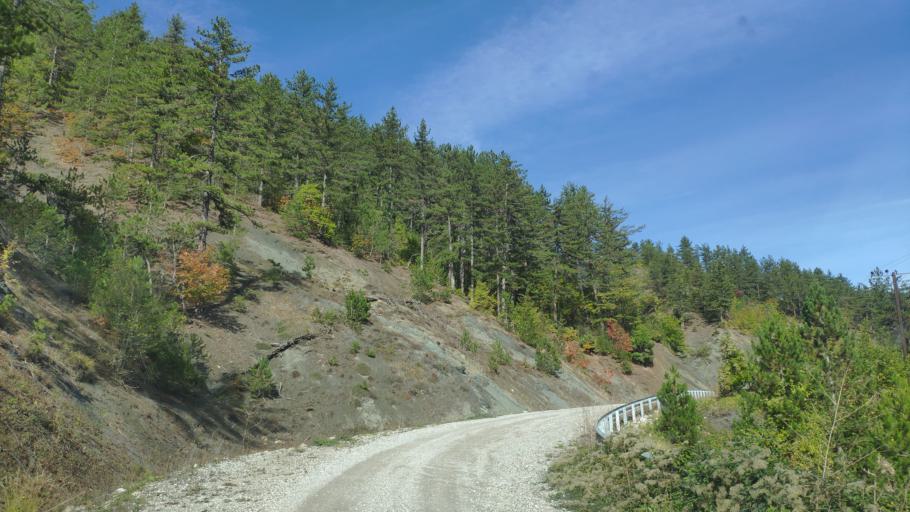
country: AL
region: Korce
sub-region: Rrethi i Devollit
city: Miras
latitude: 40.4164
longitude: 20.8706
